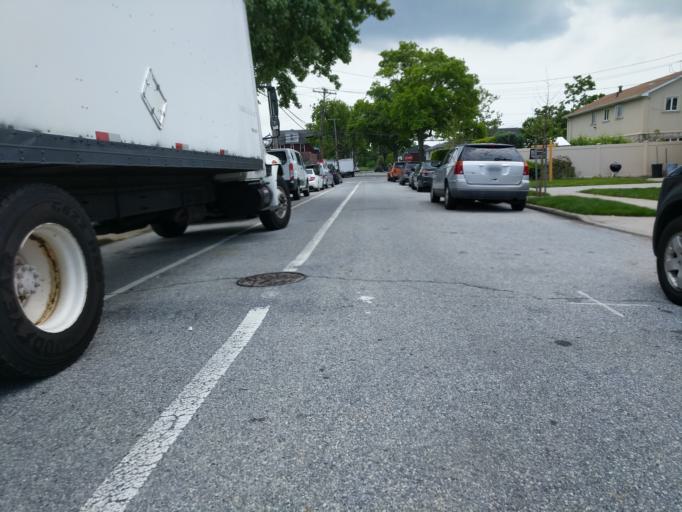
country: US
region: New York
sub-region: Queens County
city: Borough of Queens
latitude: 40.6512
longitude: -73.8399
